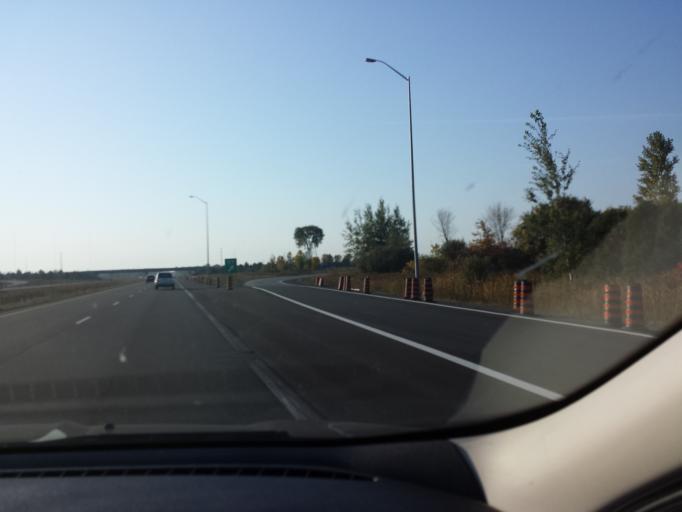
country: CA
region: Ontario
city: Bells Corners
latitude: 45.2135
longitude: -75.7404
